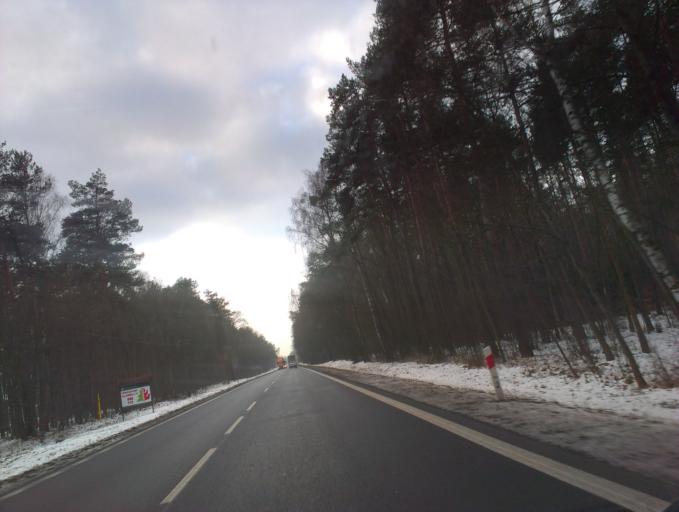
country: PL
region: Greater Poland Voivodeship
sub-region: Powiat zlotowski
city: Jastrowie
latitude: 53.4377
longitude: 16.8362
